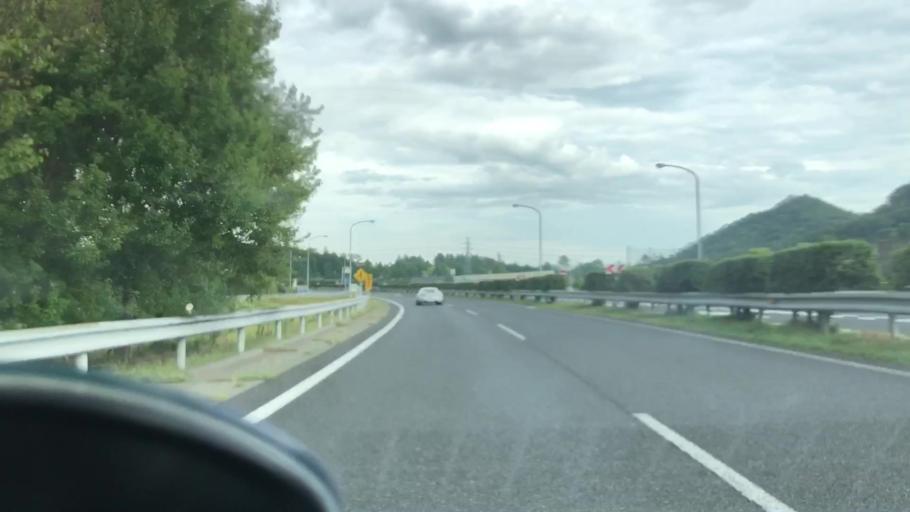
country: JP
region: Hyogo
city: Yashiro
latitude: 34.9345
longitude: 134.8645
